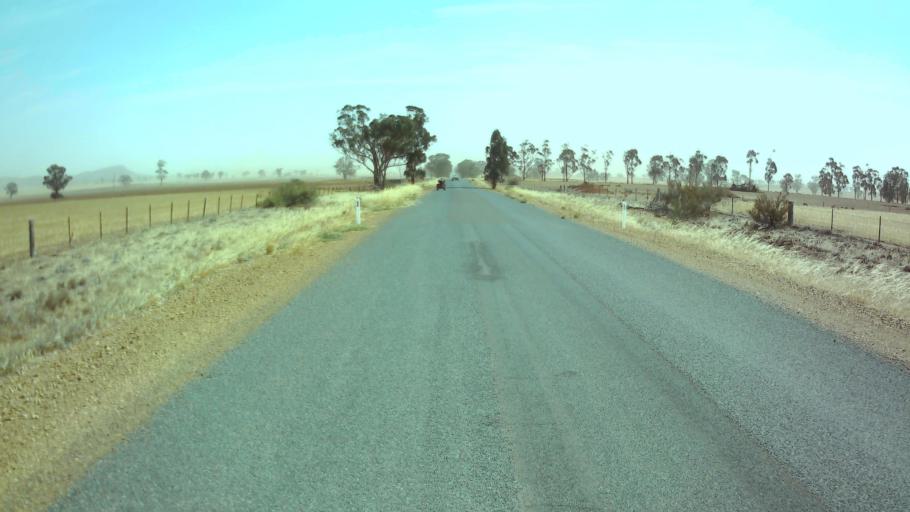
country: AU
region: New South Wales
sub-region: Weddin
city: Grenfell
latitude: -33.7676
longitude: 147.9875
